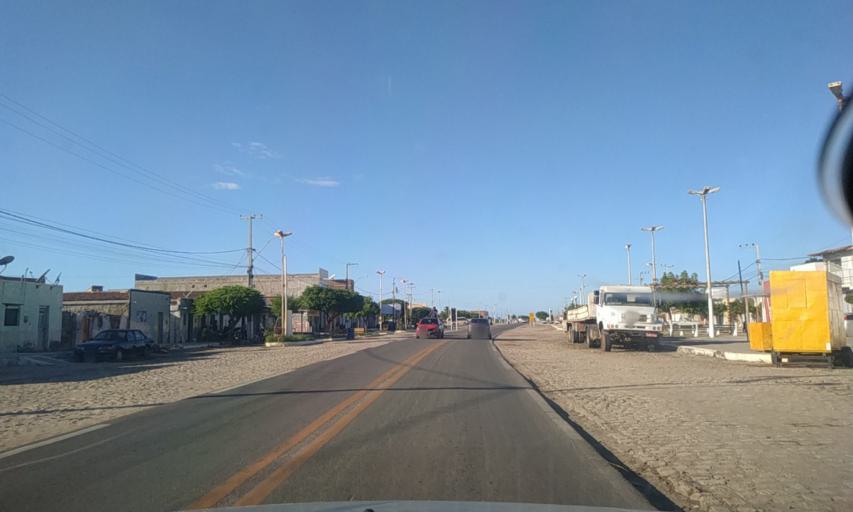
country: BR
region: Rio Grande do Norte
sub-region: Areia Branca
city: Areia Branca
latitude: -4.9517
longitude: -37.1272
